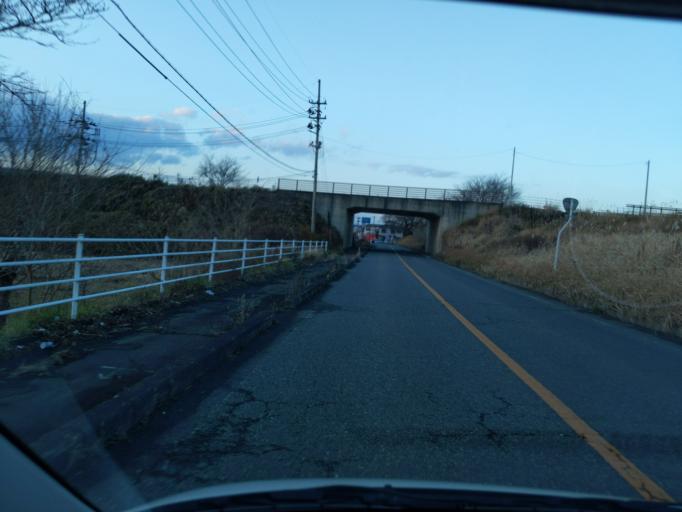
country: JP
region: Iwate
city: Ichinoseki
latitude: 38.7629
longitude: 141.1334
